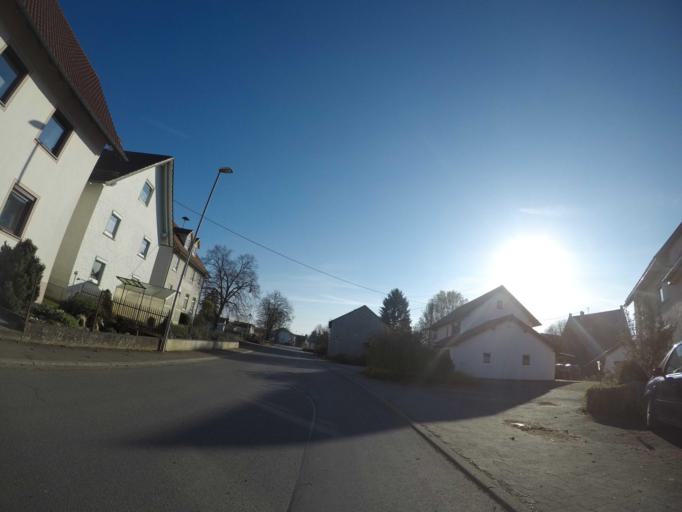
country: DE
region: Baden-Wuerttemberg
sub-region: Tuebingen Region
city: Grundsheim
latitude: 48.1784
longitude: 9.6675
